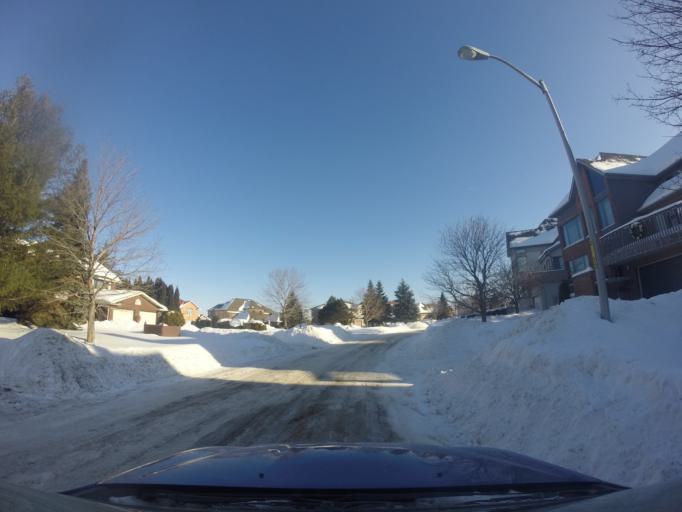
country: CA
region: Ontario
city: Greater Sudbury
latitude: 46.4582
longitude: -80.9892
